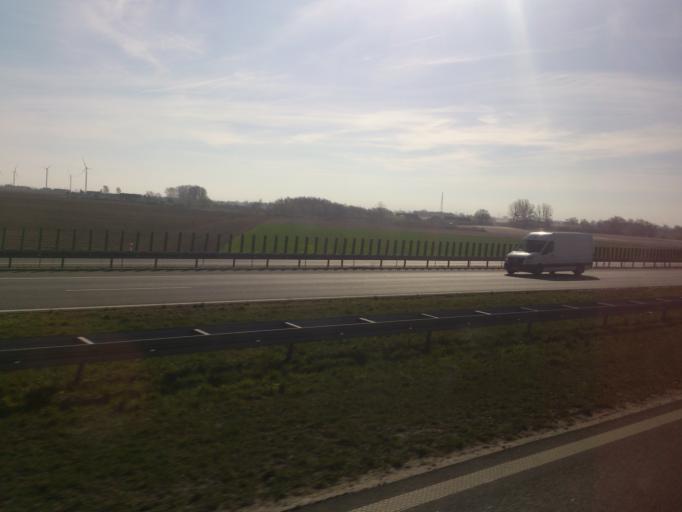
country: PL
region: Kujawsko-Pomorskie
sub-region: Powiat aleksandrowski
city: Raciazek
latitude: 52.8174
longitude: 18.8077
